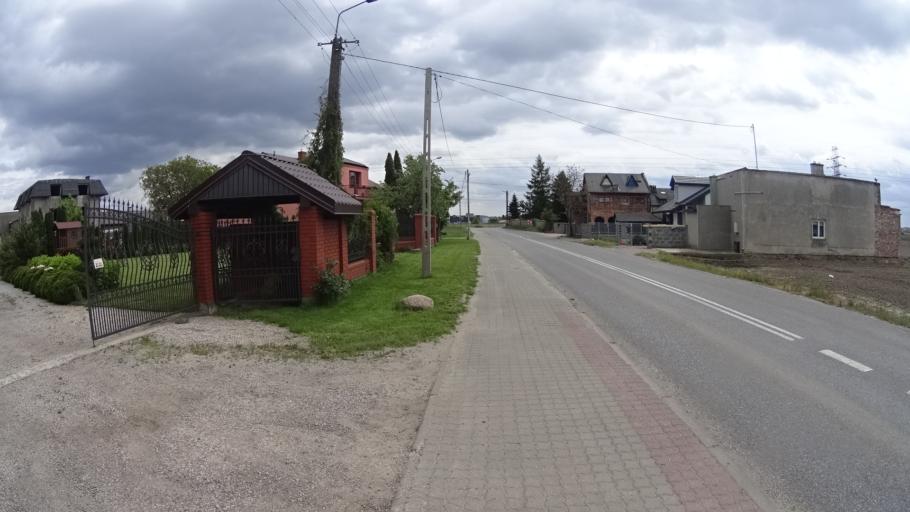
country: PL
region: Masovian Voivodeship
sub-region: Powiat warszawski zachodni
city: Babice
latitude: 52.2248
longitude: 20.8325
